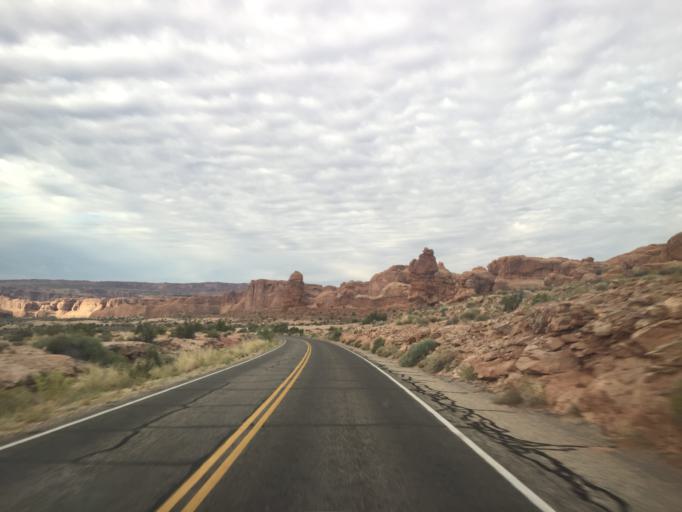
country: US
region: Utah
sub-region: Grand County
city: Moab
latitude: 38.6873
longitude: -109.5802
